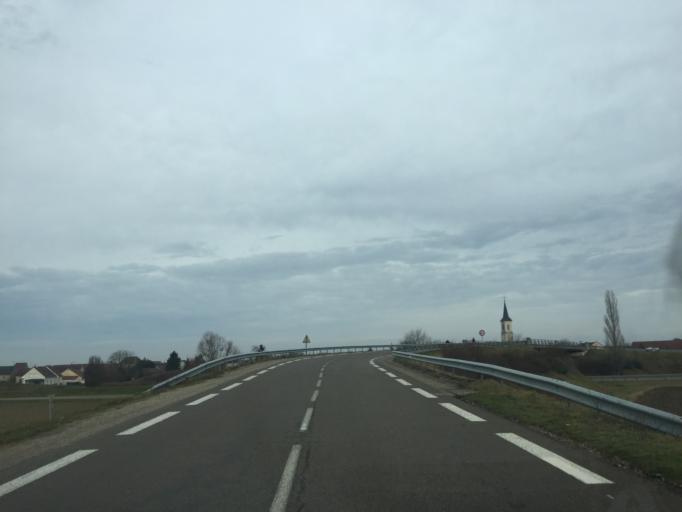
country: FR
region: Franche-Comte
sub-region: Departement du Jura
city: Tavaux
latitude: 47.0306
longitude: 5.4081
